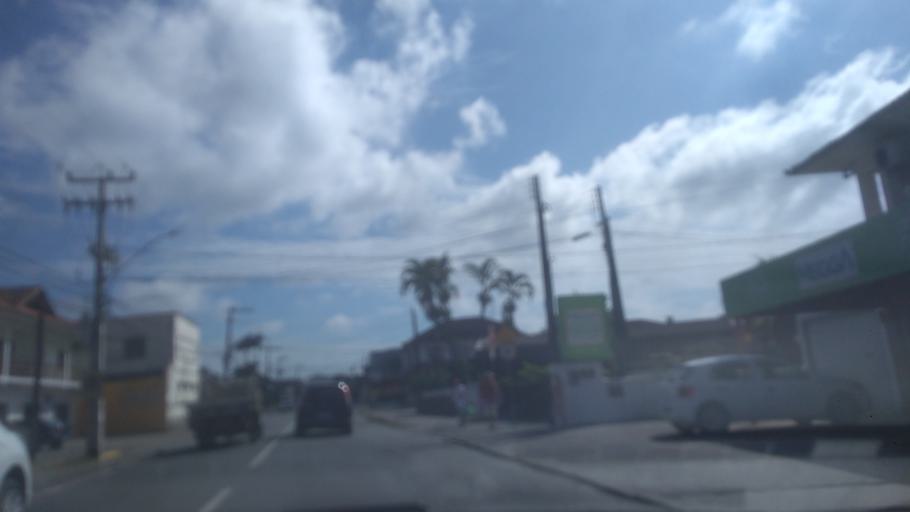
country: BR
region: Santa Catarina
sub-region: Joinville
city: Joinville
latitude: -26.2999
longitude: -48.8213
